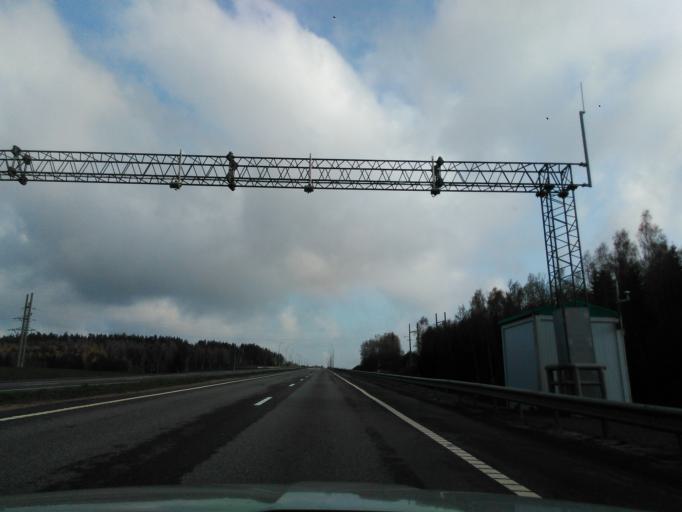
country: BY
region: Minsk
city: Lahoysk
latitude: 54.1840
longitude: 27.8171
